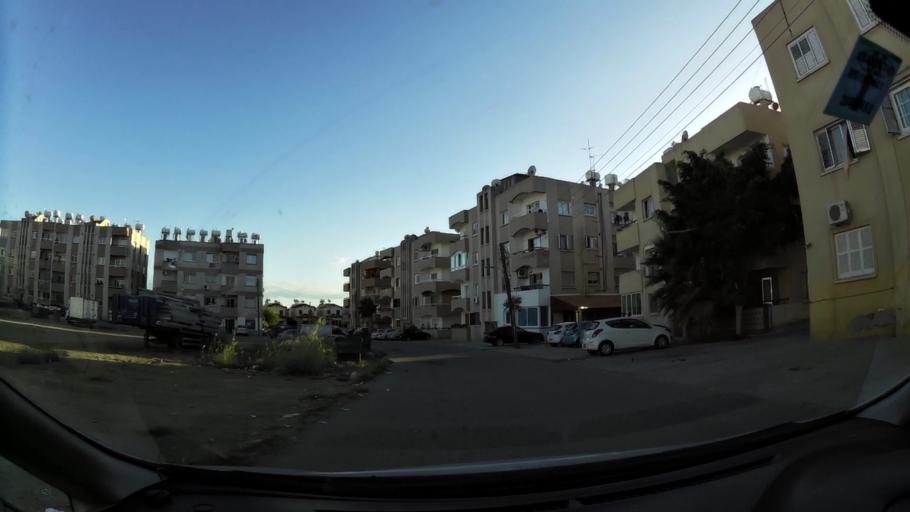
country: CY
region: Lefkosia
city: Nicosia
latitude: 35.2049
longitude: 33.3274
